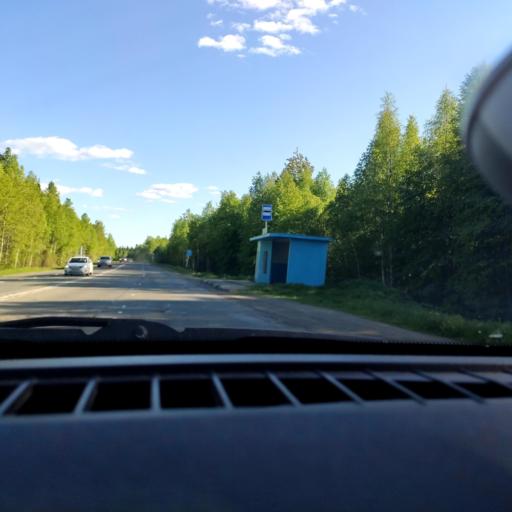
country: RU
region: Perm
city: Perm
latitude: 58.2461
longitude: 56.1585
